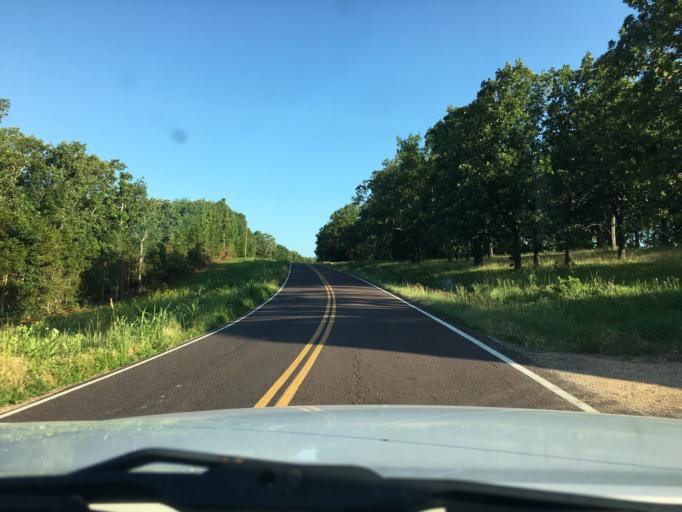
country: US
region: Missouri
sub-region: Gasconade County
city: Owensville
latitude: 38.4478
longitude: -91.6318
